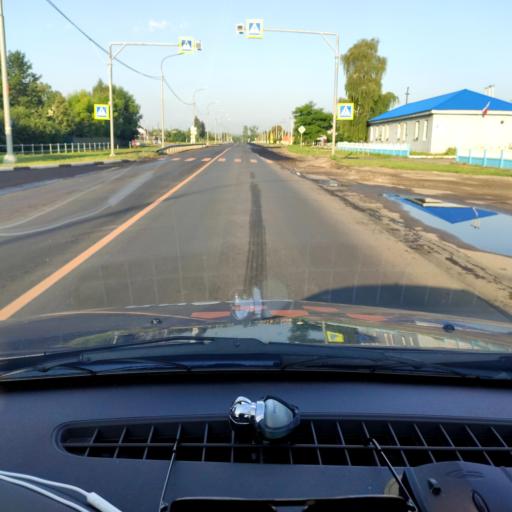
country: RU
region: Lipetsk
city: Izmalkovo
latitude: 52.4936
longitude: 38.0542
